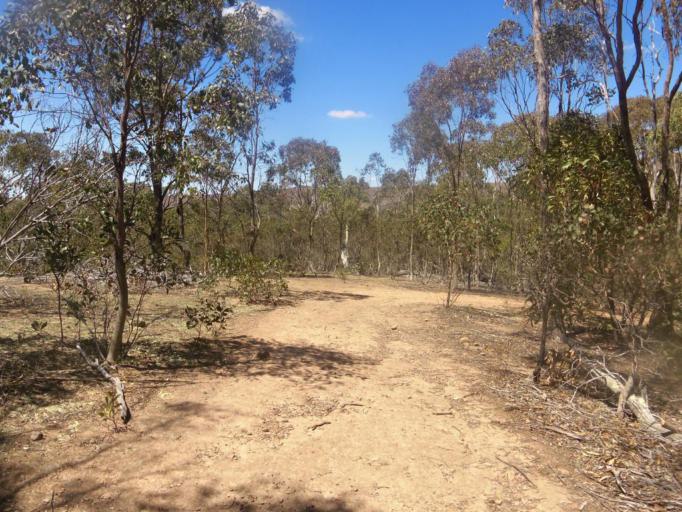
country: AU
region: Victoria
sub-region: Moorabool
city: Bacchus Marsh
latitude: -37.6663
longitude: 144.3592
